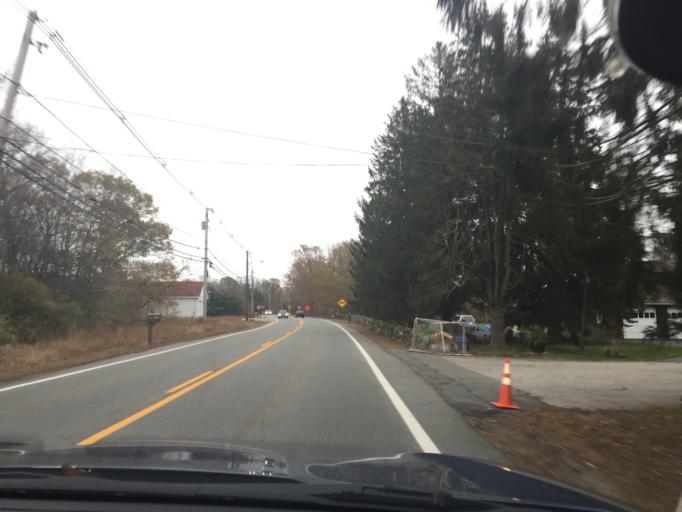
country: US
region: Rhode Island
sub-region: Providence County
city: North Scituate
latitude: 41.8167
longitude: -71.6640
